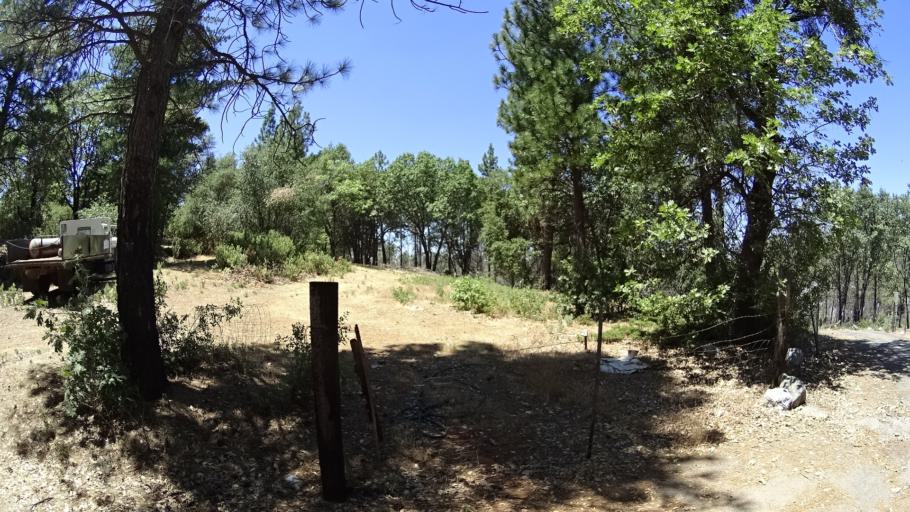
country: US
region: California
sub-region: Calaveras County
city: Mountain Ranch
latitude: 38.2536
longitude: -120.5305
